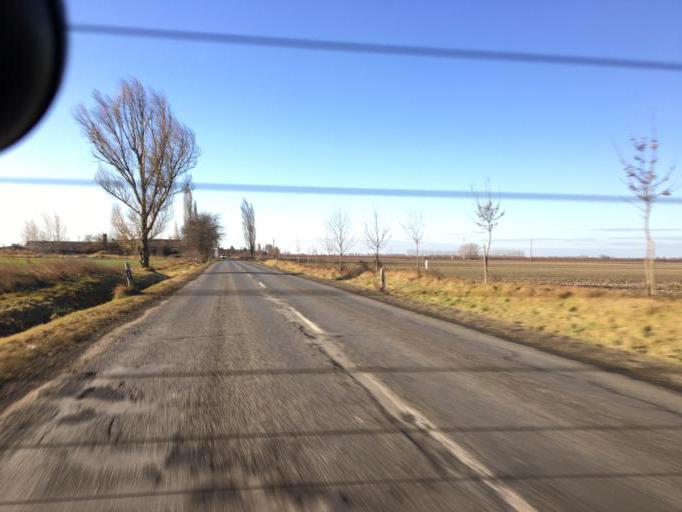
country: HU
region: Pest
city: Kiskunlachaza
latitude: 47.1736
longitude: 18.9882
